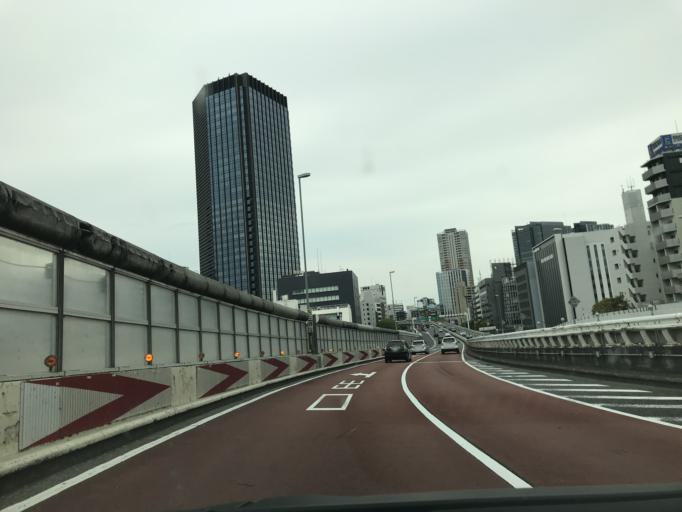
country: JP
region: Tokyo
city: Tokyo
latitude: 35.7075
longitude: 139.7434
